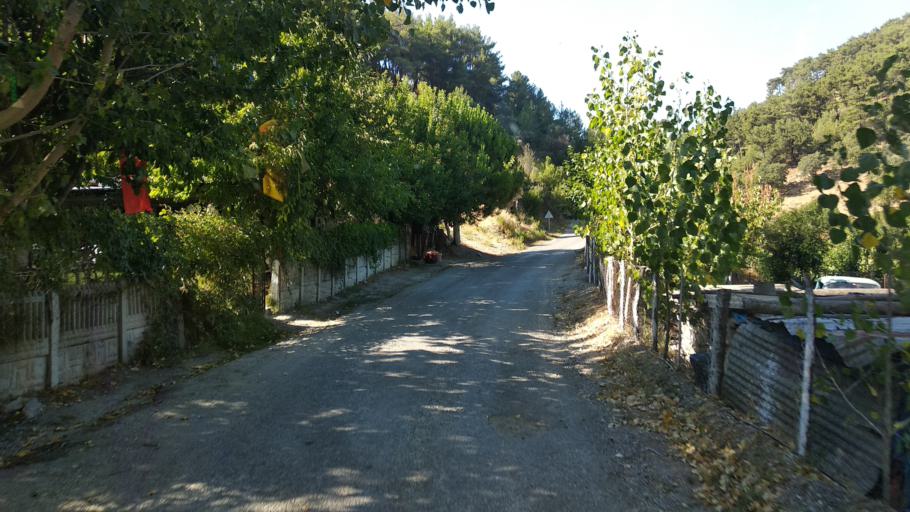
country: TR
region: Izmir
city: Gaziemir
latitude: 38.3245
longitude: 26.9571
